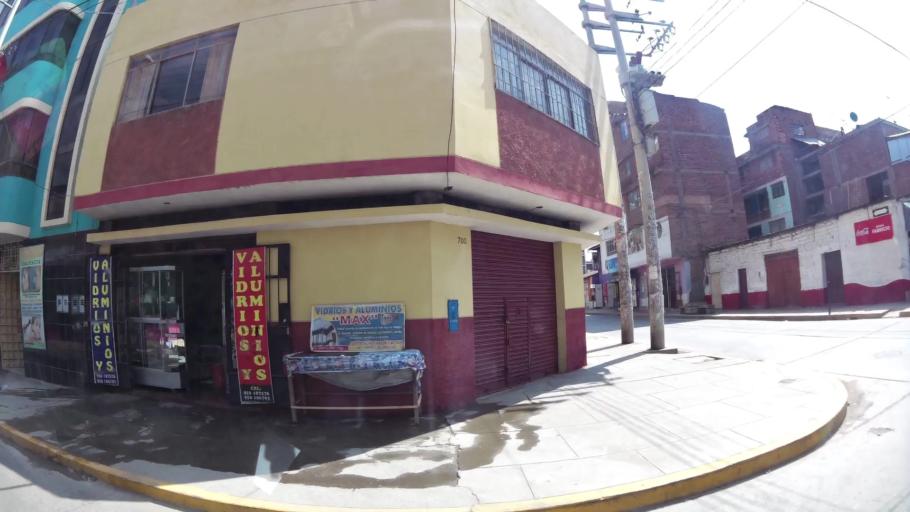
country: PE
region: Junin
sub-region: Provincia de Huancayo
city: El Tambo
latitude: -12.0712
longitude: -75.2132
